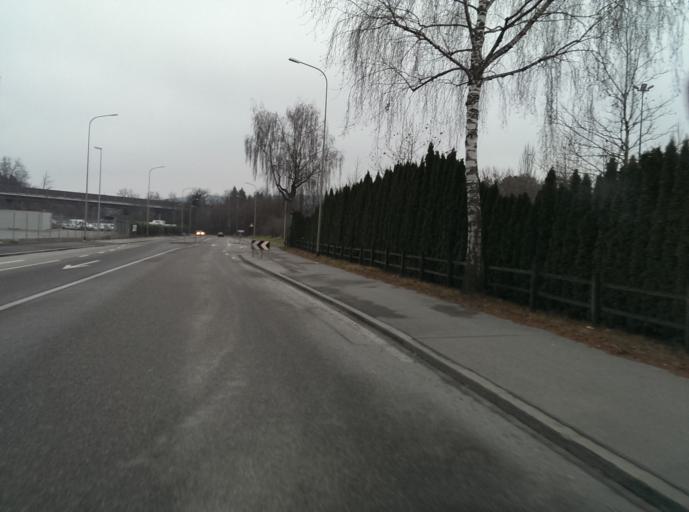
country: CH
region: Zurich
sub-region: Bezirk Dietikon
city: Dietikon / Hofacker
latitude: 47.4034
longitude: 8.4172
